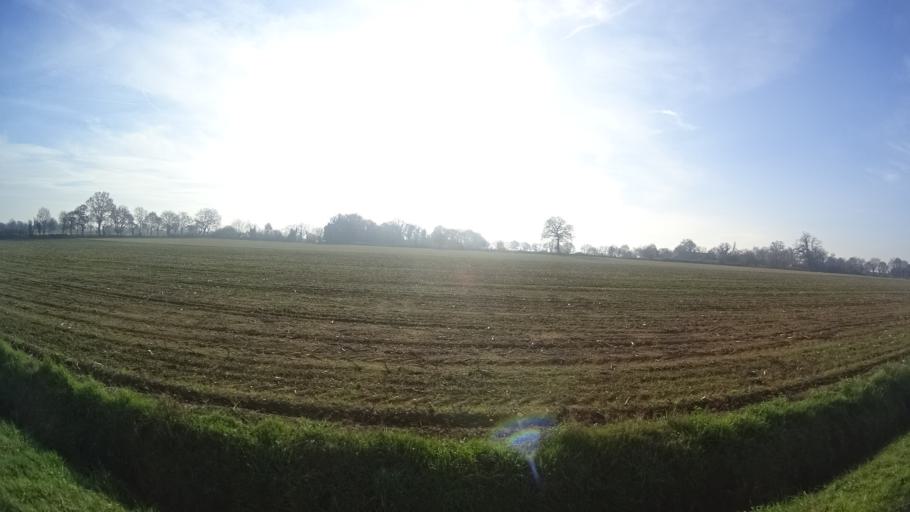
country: FR
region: Brittany
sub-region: Departement du Morbihan
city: Rieux
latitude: 47.5975
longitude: -2.1287
